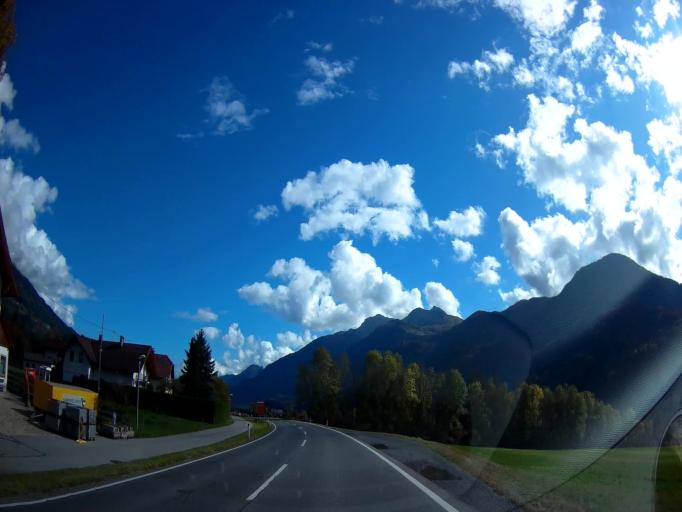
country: AT
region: Carinthia
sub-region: Politischer Bezirk Spittal an der Drau
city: Oberdrauburg
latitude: 46.7474
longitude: 12.9927
